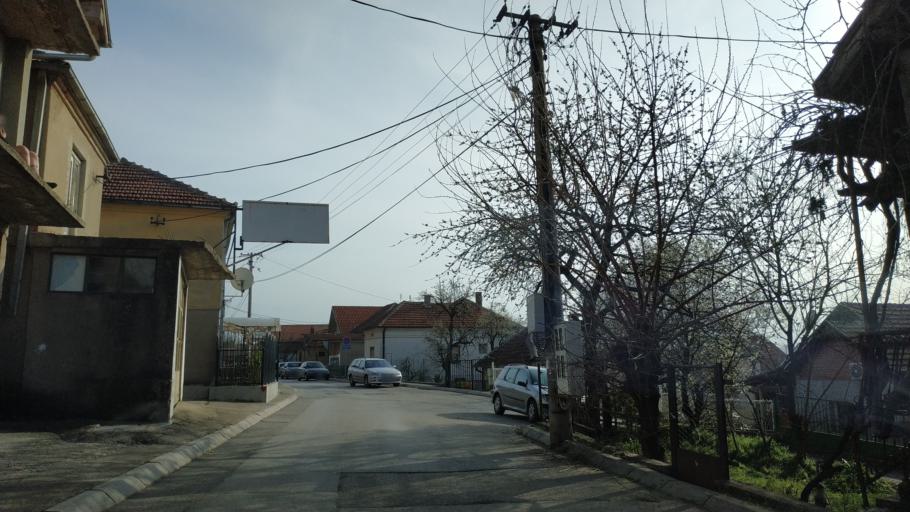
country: RS
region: Central Serbia
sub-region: Nisavski Okrug
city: Aleksinac
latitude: 43.5422
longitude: 21.7167
